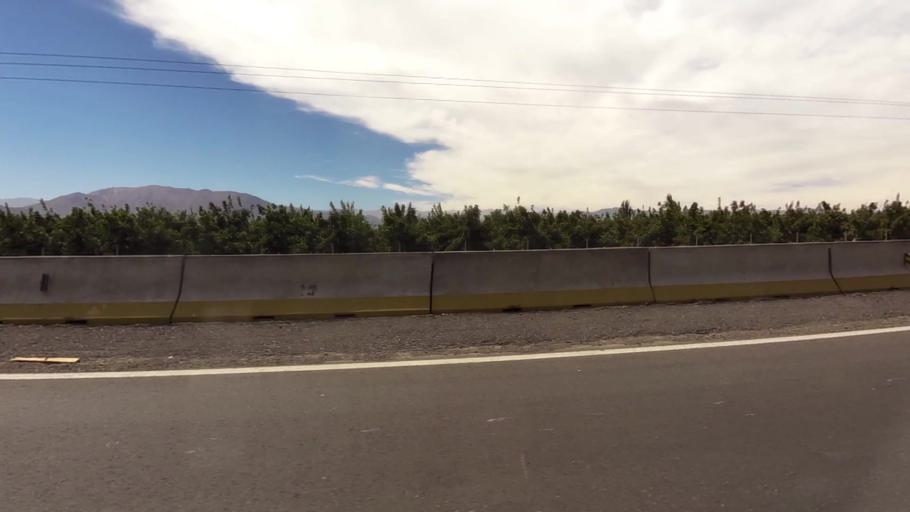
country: CL
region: O'Higgins
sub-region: Provincia de Cachapoal
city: Graneros
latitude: -34.0127
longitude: -70.7033
